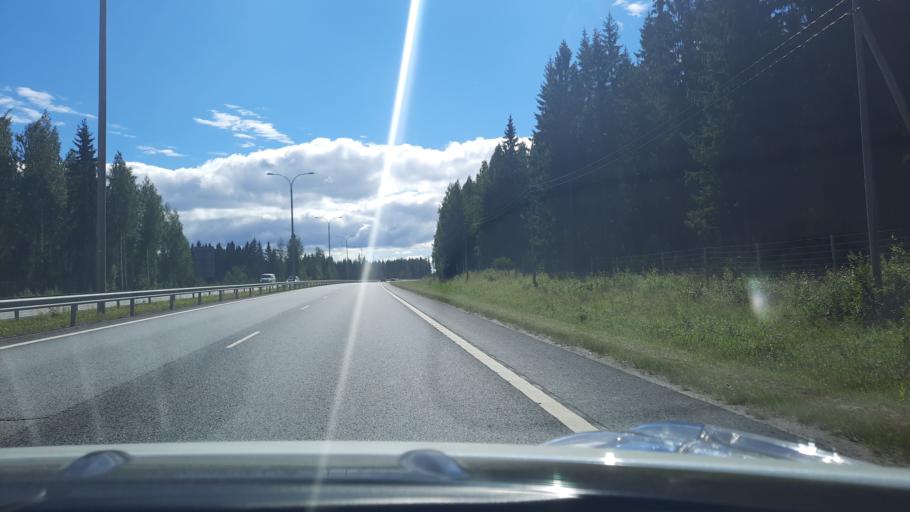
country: FI
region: North Karelia
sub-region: Joensuu
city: Joensuu
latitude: 62.5805
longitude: 29.8285
